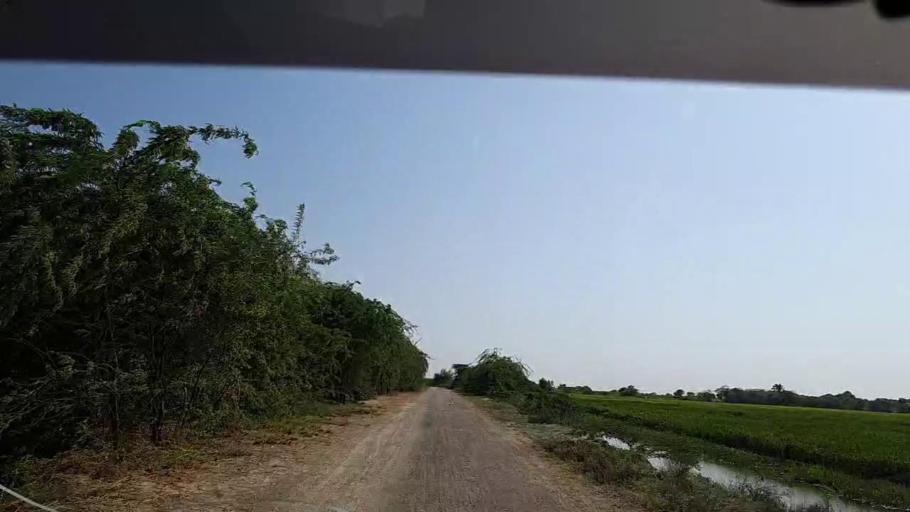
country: PK
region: Sindh
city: Badin
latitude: 24.6287
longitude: 68.7829
